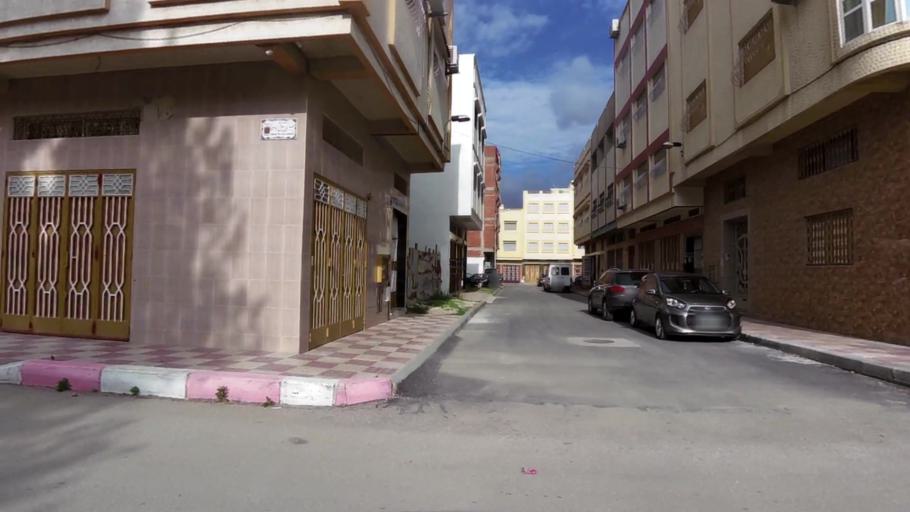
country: MA
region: Tanger-Tetouan
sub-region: Tanger-Assilah
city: Tangier
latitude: 35.7510
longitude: -5.7972
